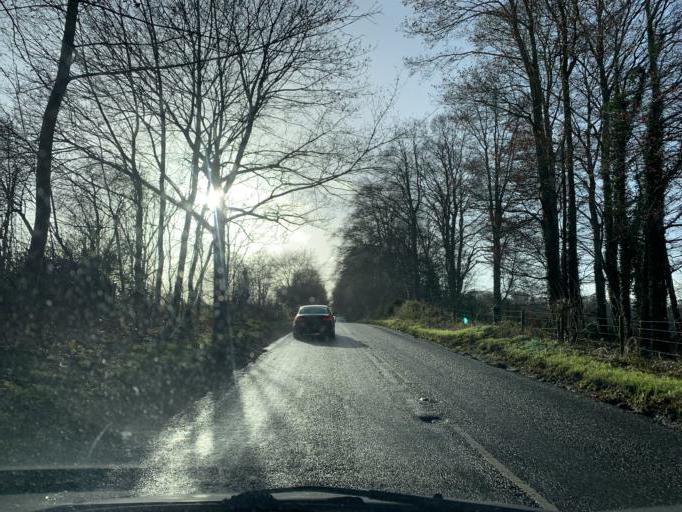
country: GB
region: England
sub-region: Wiltshire
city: Winterbourne Stoke
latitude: 51.1613
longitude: -1.8591
